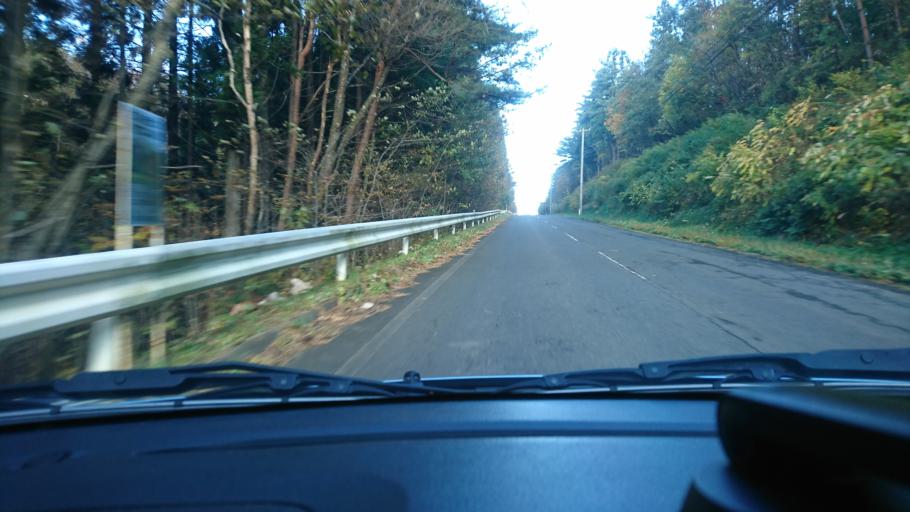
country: JP
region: Iwate
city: Ichinoseki
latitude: 38.8025
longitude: 141.2582
